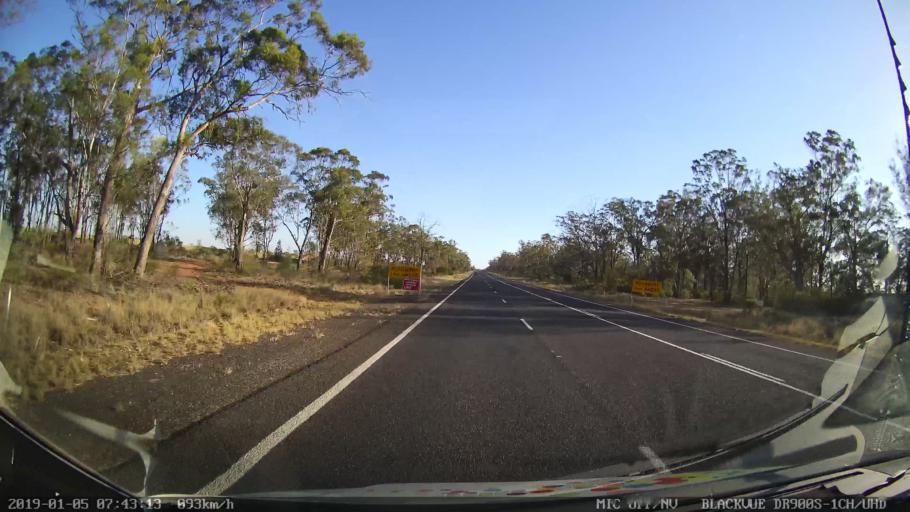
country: AU
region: New South Wales
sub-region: Gilgandra
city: Gilgandra
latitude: -31.8879
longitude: 148.6323
